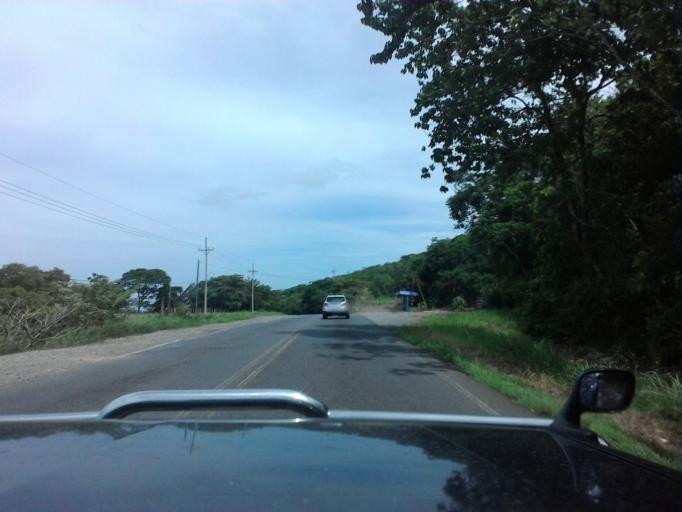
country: CR
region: Puntarenas
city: Esparza
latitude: 10.0154
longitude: -84.6123
